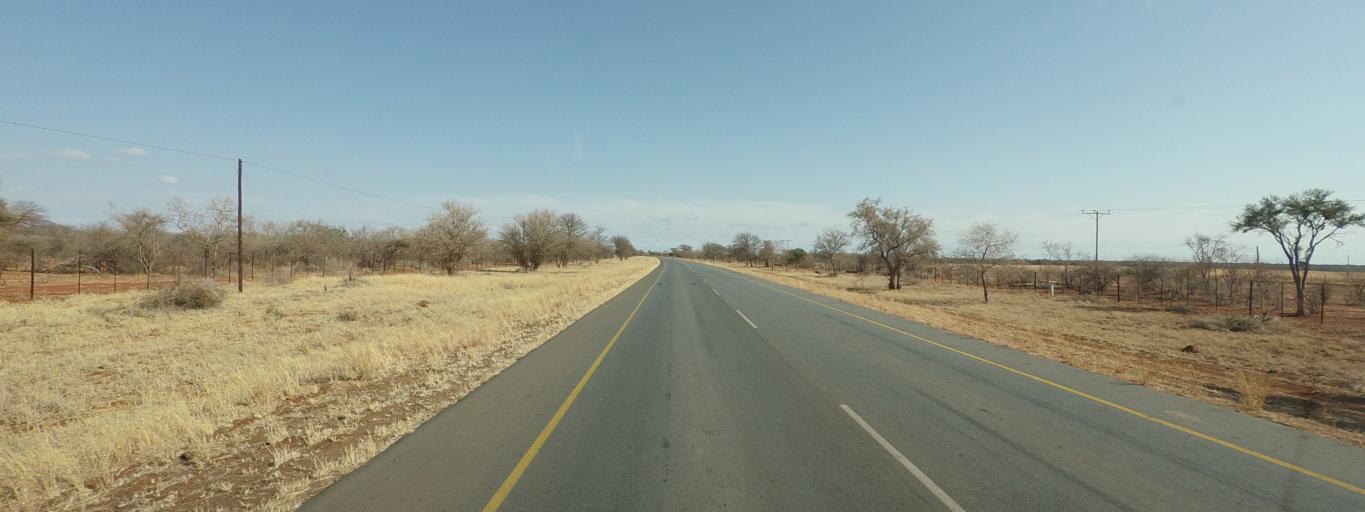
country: BW
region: Central
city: Makobeng
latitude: -22.9721
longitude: 27.9136
